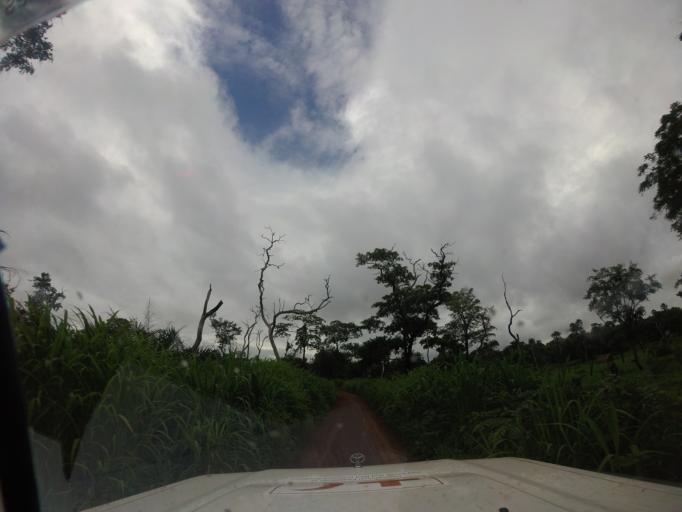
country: SL
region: Northern Province
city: Kamakwie
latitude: 9.6592
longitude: -12.2197
